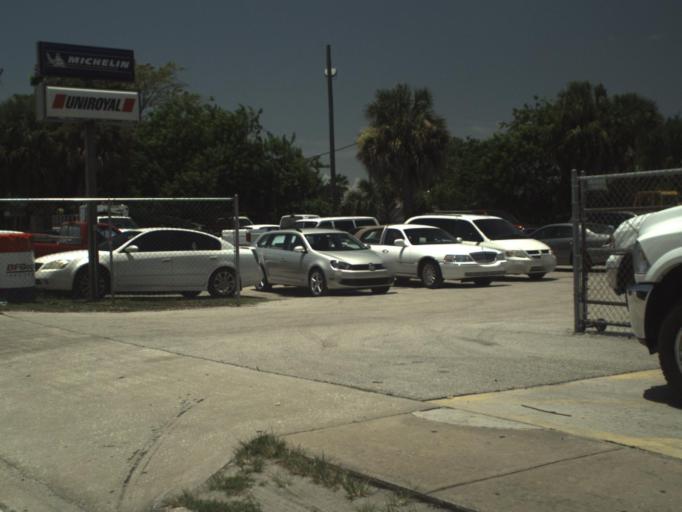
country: US
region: Florida
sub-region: Martin County
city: Stuart
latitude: 27.1800
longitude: -80.2367
